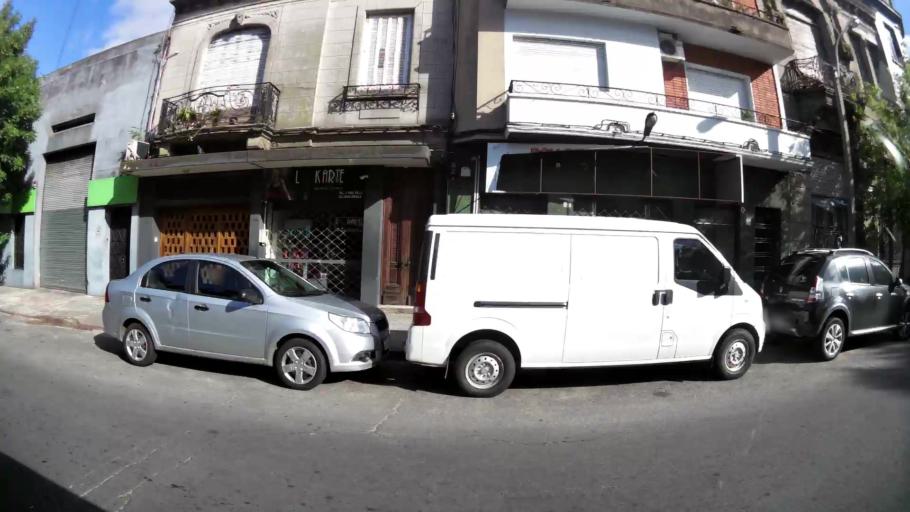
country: UY
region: Montevideo
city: Montevideo
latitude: -34.8931
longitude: -56.1765
